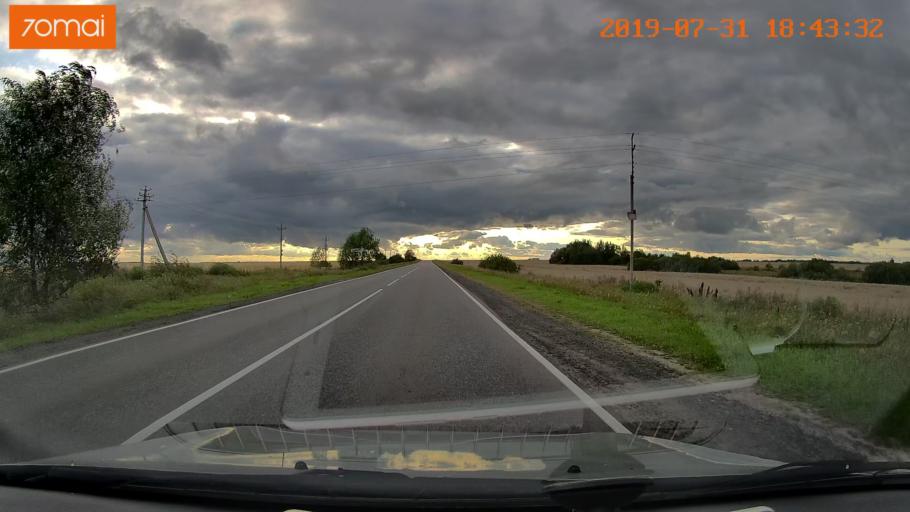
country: RU
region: Moskovskaya
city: Troitskoye
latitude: 55.2451
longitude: 38.5734
